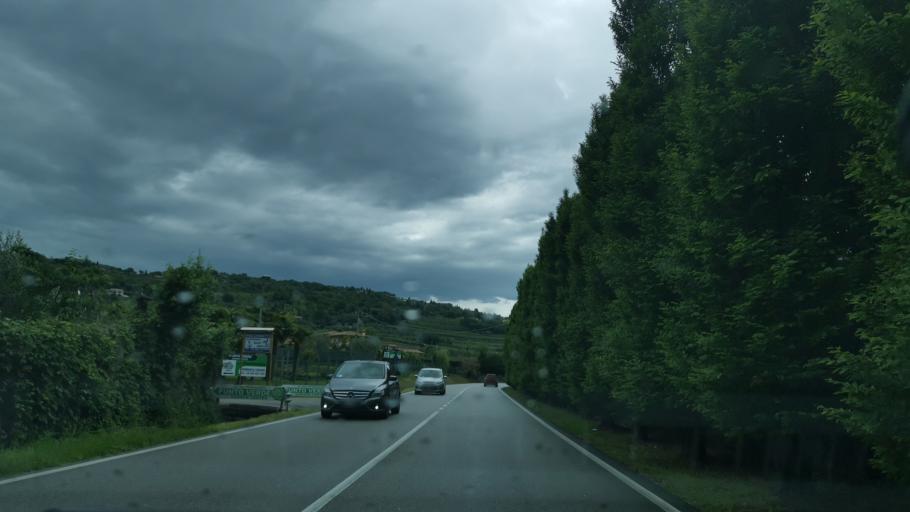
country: IT
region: Veneto
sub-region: Provincia di Verona
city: Bardolino
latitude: 45.5445
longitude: 10.7364
